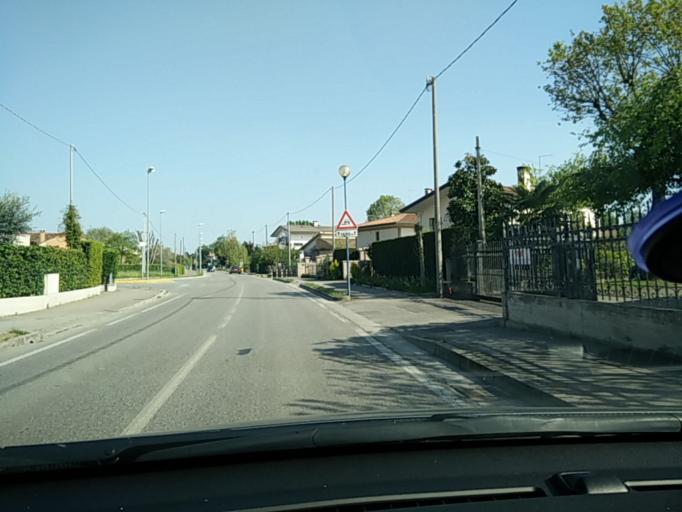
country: IT
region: Veneto
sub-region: Provincia di Treviso
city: Sant'Alberto
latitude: 45.6110
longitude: 12.1387
